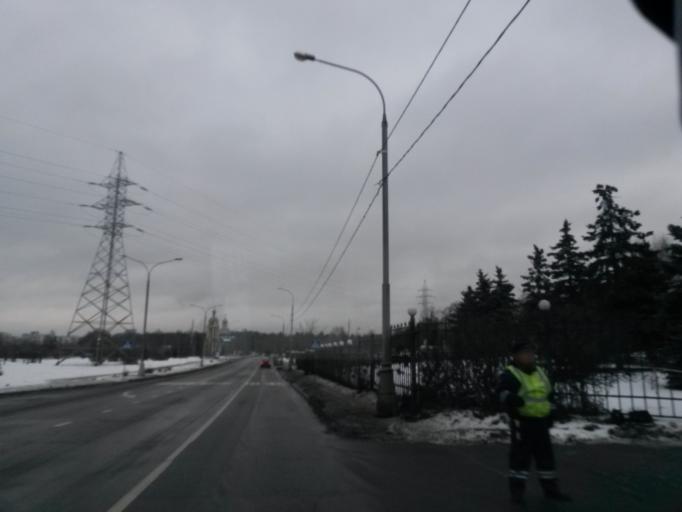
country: RU
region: Moskovskaya
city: Bol'shaya Setun'
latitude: 55.6999
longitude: 37.4074
